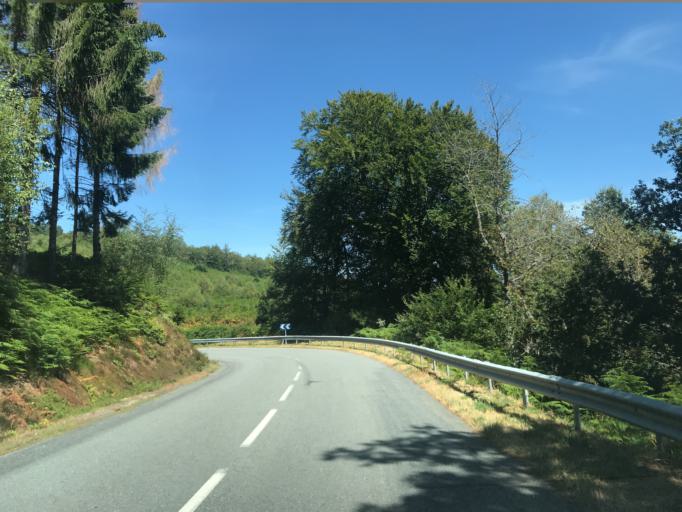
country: FR
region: Limousin
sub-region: Departement de la Creuse
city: Felletin
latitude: 45.7821
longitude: 2.1412
